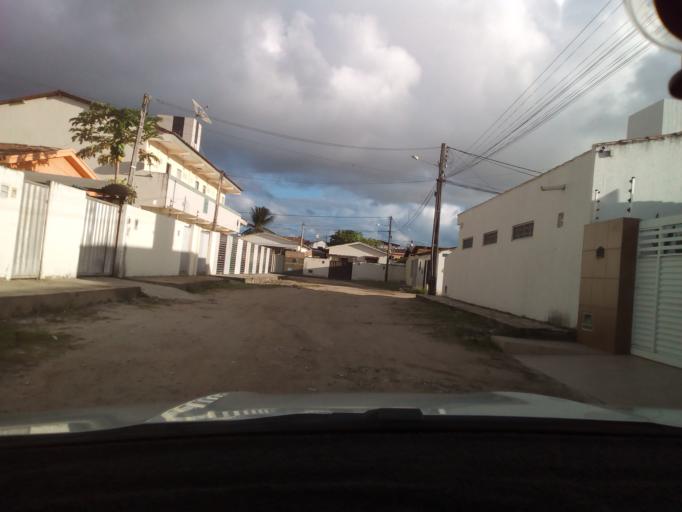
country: BR
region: Paraiba
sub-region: Joao Pessoa
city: Joao Pessoa
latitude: -7.1793
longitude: -34.8355
